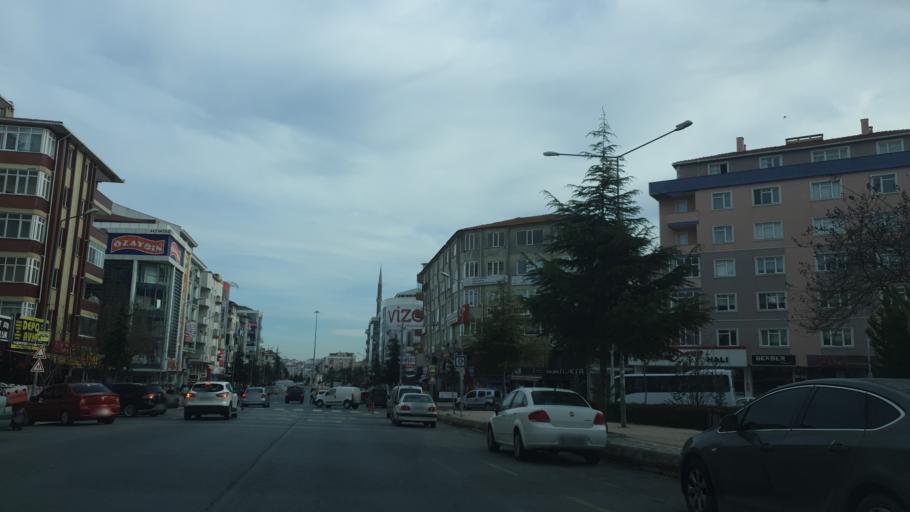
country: TR
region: Tekirdag
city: Cerkezkoey
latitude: 41.2891
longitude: 27.9988
